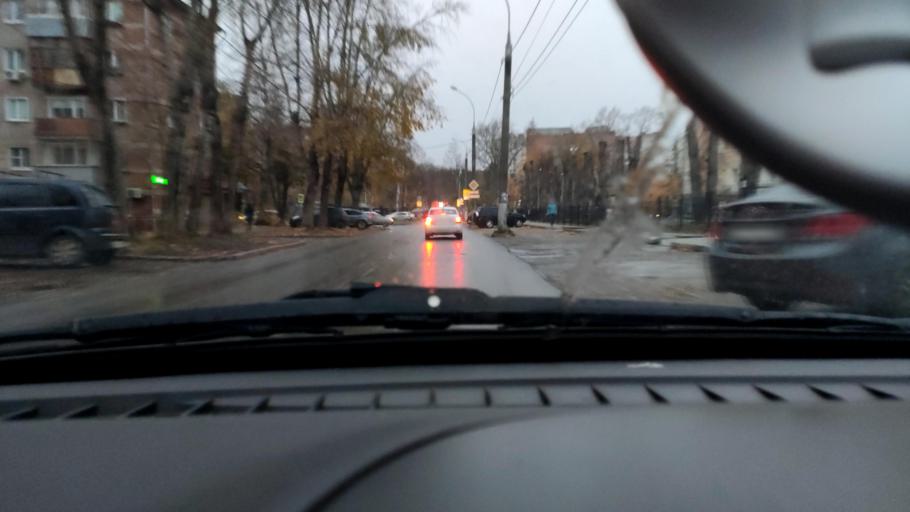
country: RU
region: Perm
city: Perm
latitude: 57.9836
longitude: 56.1902
